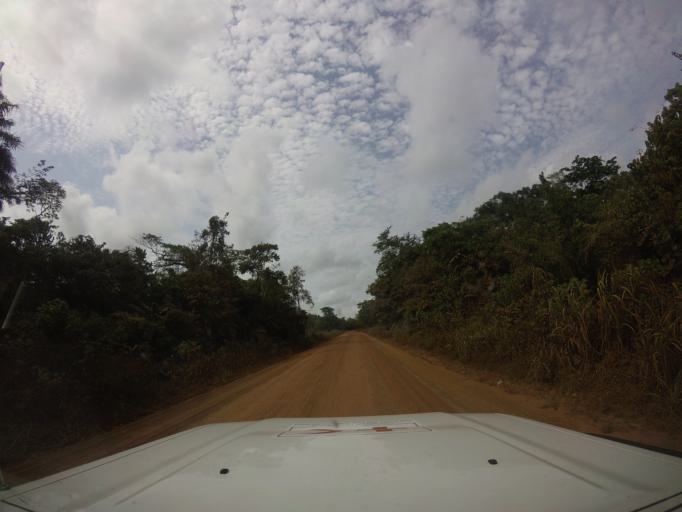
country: LR
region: Grand Cape Mount
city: Robertsport
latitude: 6.7067
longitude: -11.0879
